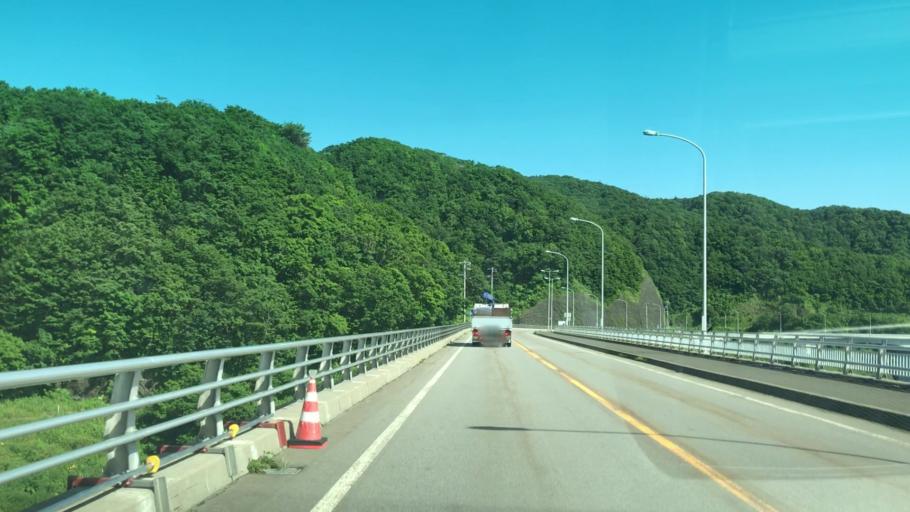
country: JP
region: Hokkaido
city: Iwanai
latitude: 43.1289
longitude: 140.4395
